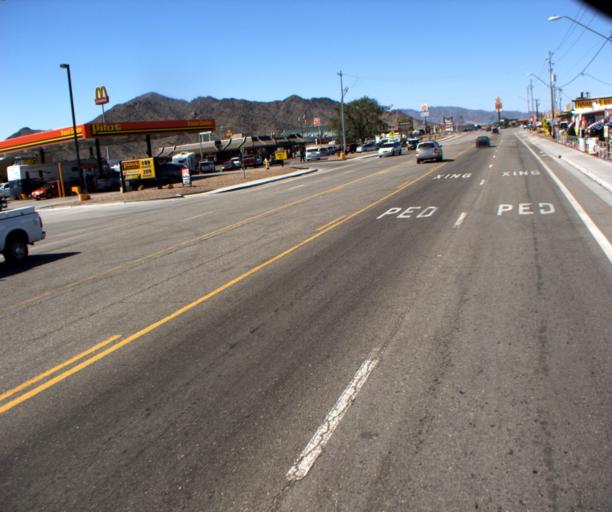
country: US
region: Arizona
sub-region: La Paz County
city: Quartzsite
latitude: 33.6624
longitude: -114.2364
